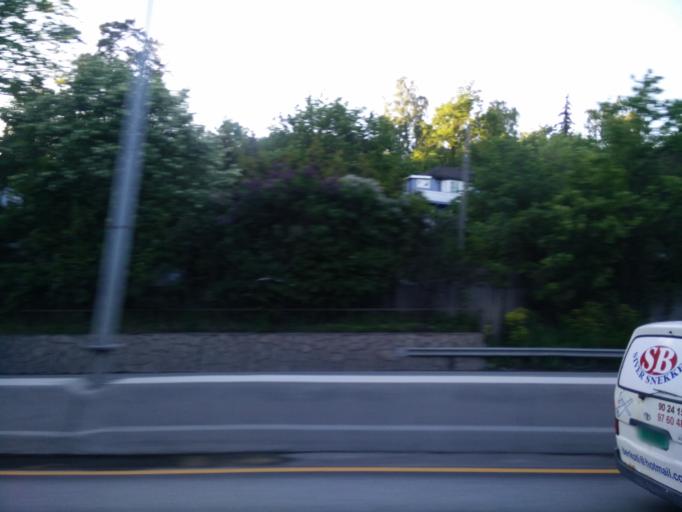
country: NO
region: Akershus
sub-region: Baerum
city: Sandvika
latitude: 59.8949
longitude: 10.5540
